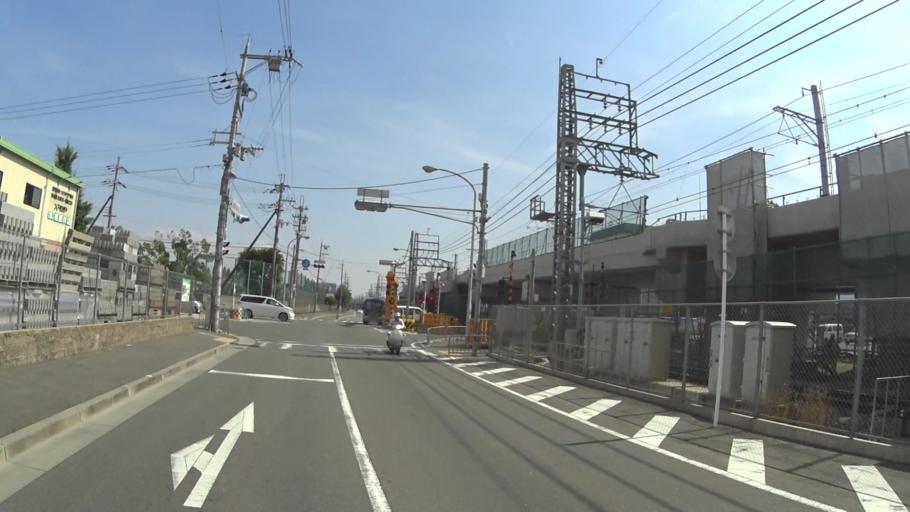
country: JP
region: Kyoto
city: Muko
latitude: 34.9733
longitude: 135.7032
